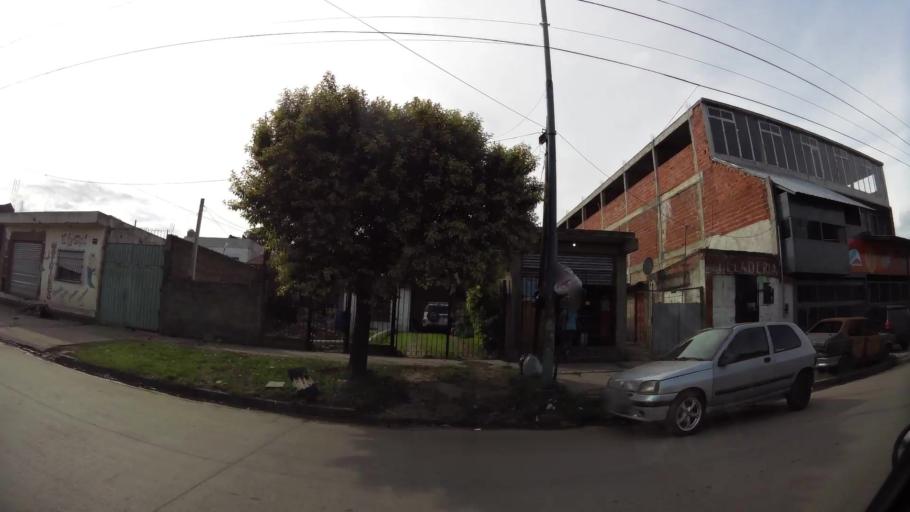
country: AR
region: Buenos Aires
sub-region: Partido de Quilmes
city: Quilmes
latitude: -34.7669
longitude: -58.2542
